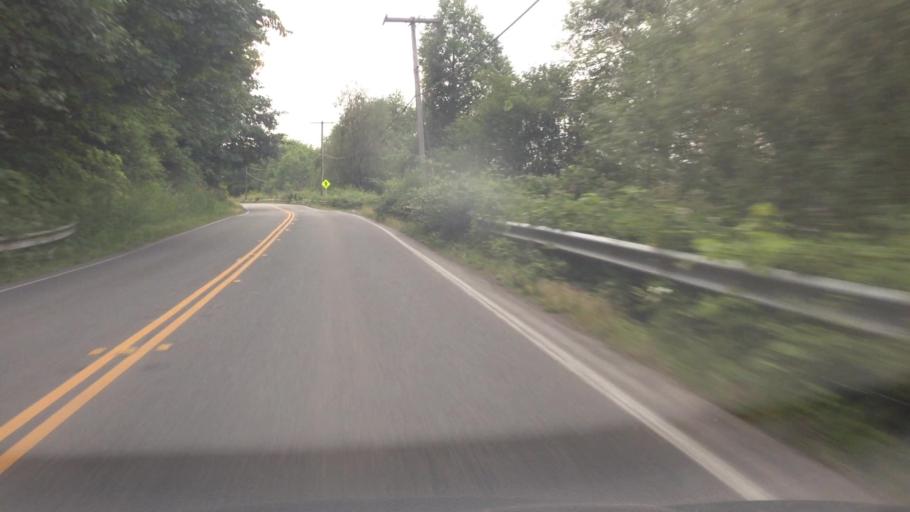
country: US
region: Washington
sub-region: King County
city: Duvall
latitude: 47.7495
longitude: -121.9641
